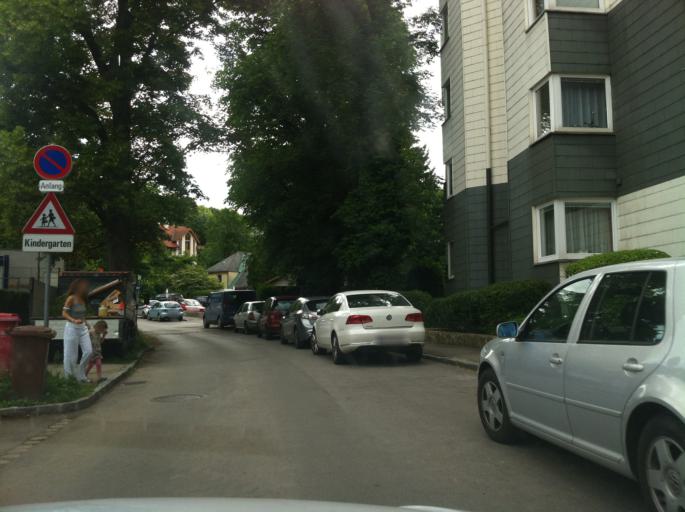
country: AT
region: Lower Austria
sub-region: Politischer Bezirk Wien-Umgebung
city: Purkersdorf
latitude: 48.2095
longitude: 16.1761
